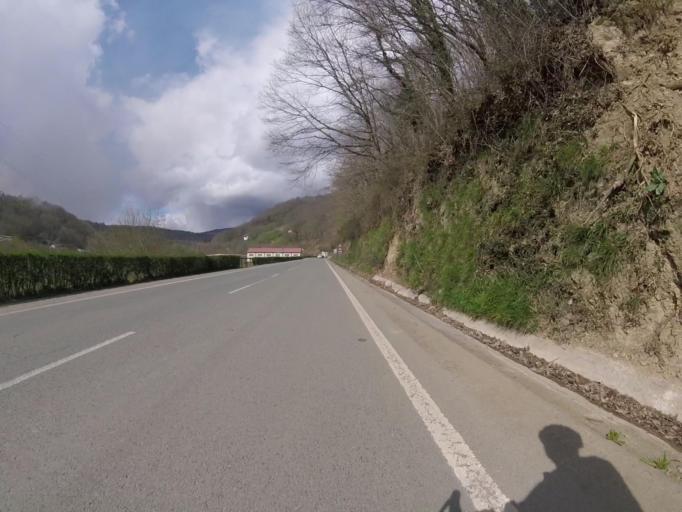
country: ES
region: Navarre
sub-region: Provincia de Navarra
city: Etxalar
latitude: 43.2356
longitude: -1.6397
